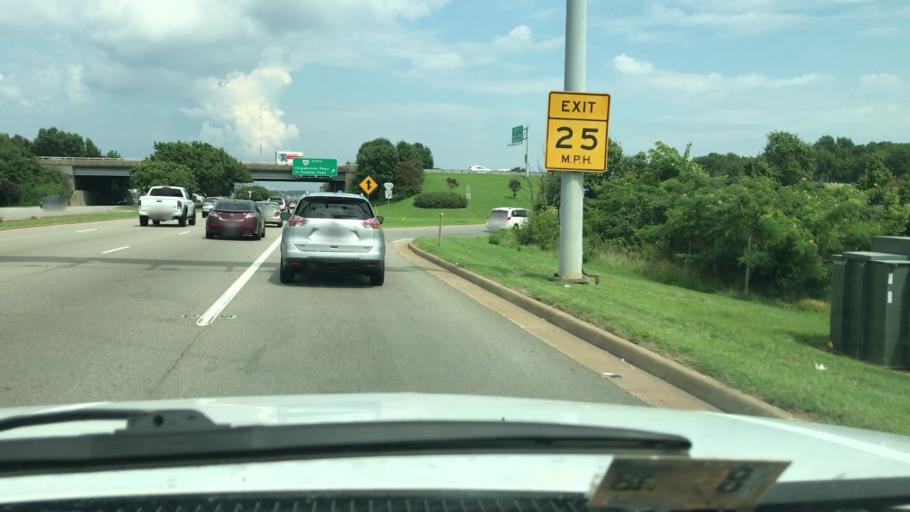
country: US
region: Virginia
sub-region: Chesterfield County
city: Bon Air
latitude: 37.5010
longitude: -77.5268
